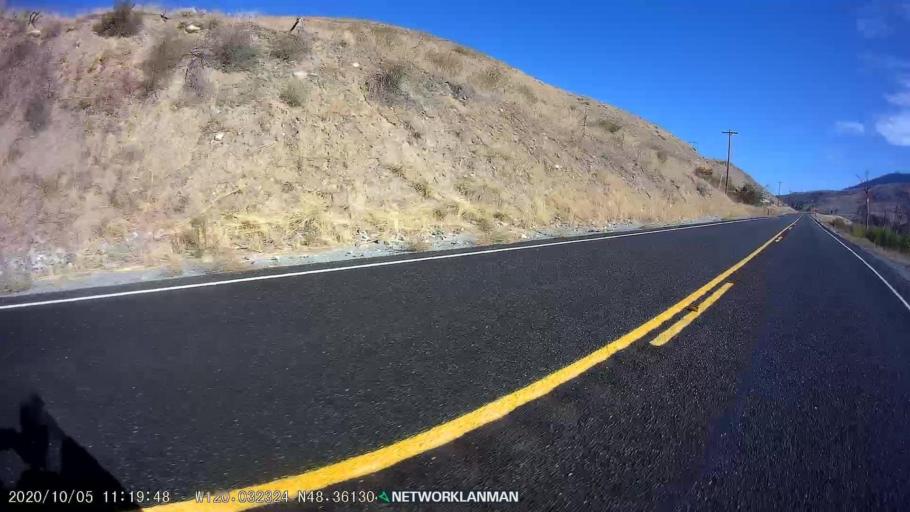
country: US
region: Washington
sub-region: Okanogan County
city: Brewster
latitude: 48.3616
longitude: -120.0321
